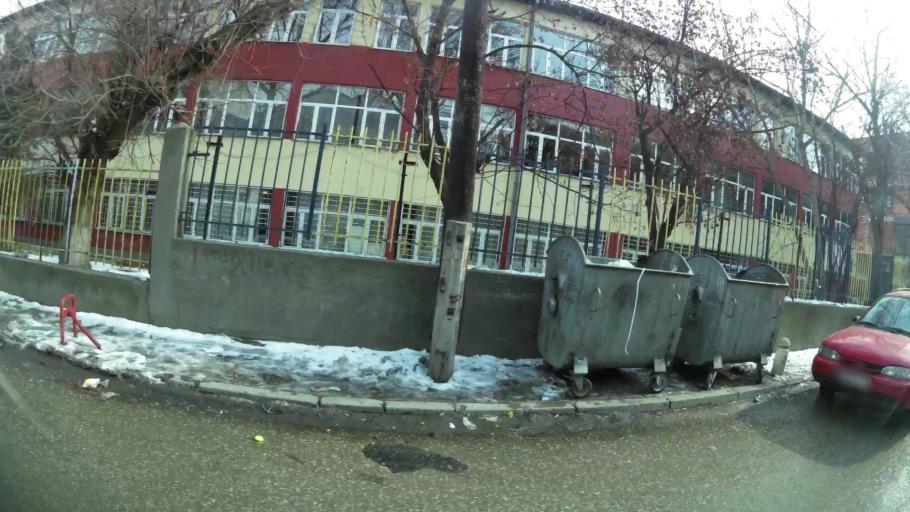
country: MK
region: Karpos
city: Skopje
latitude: 42.0051
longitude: 21.4360
